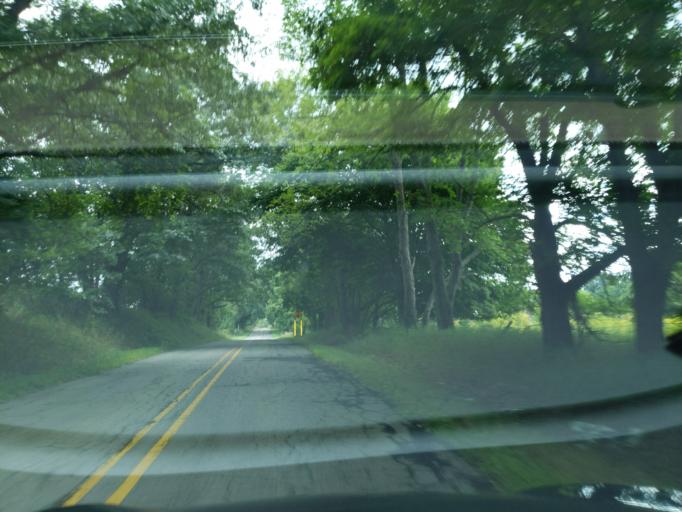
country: US
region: Michigan
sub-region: Eaton County
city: Eaton Rapids
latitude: 42.3929
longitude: -84.5808
